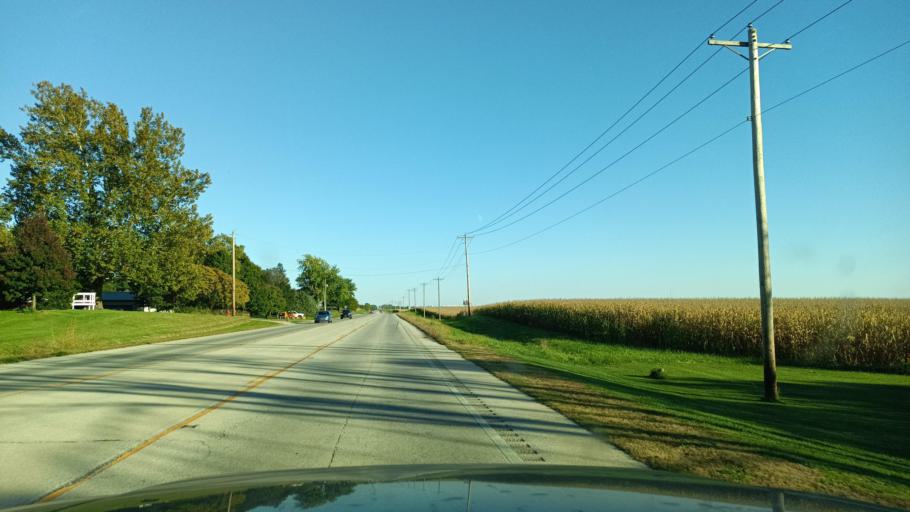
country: US
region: Illinois
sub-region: Champaign County
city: Lake of the Woods
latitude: 40.1812
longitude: -88.3581
